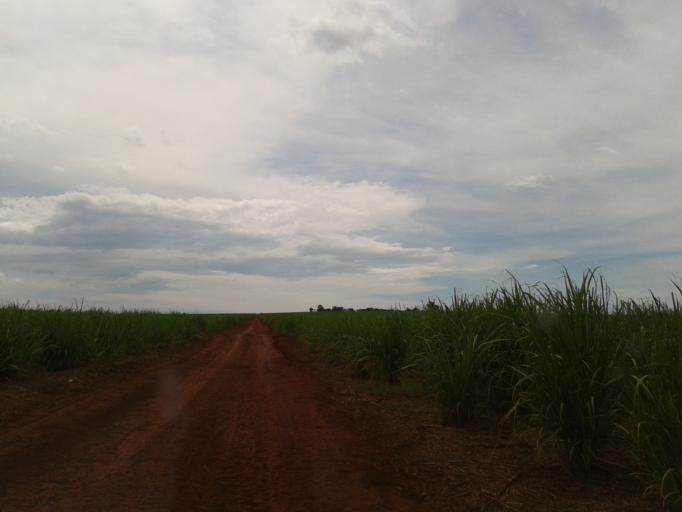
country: BR
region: Minas Gerais
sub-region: Centralina
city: Centralina
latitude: -18.6640
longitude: -49.2400
